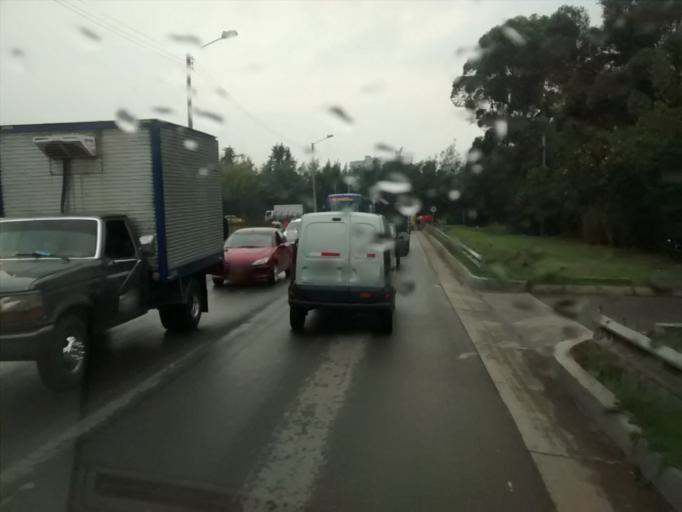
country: CO
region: Cundinamarca
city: Cota
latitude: 4.7605
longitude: -74.0929
